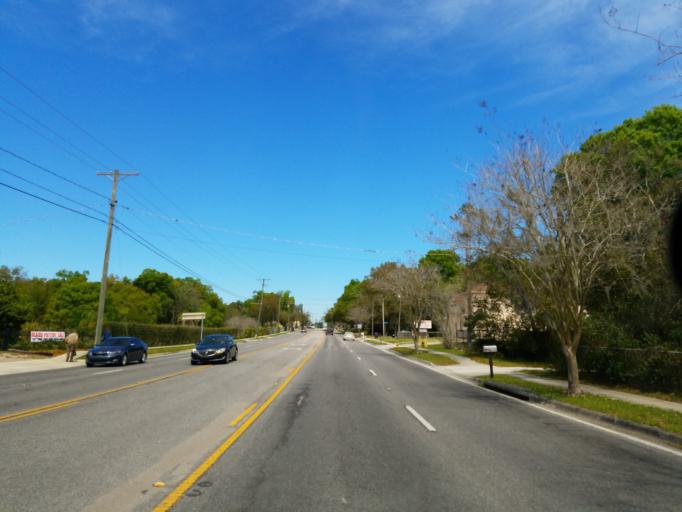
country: US
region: Florida
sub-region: Hillsborough County
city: Seffner
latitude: 27.9752
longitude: -82.2859
